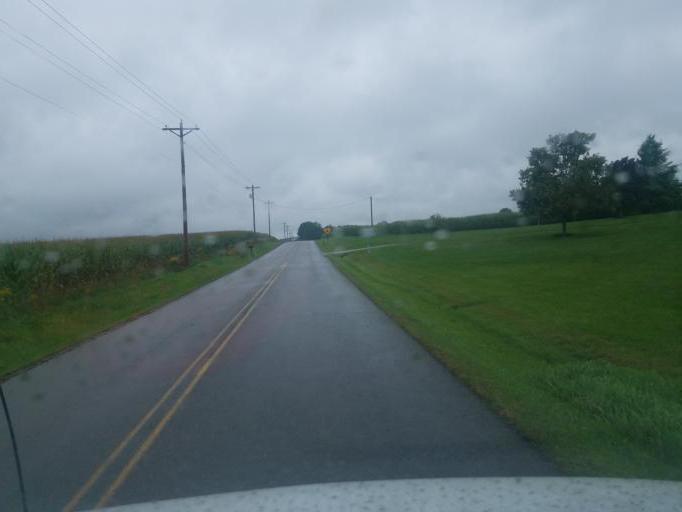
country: US
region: Ohio
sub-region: Medina County
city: Lodi
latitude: 40.9745
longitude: -81.9924
